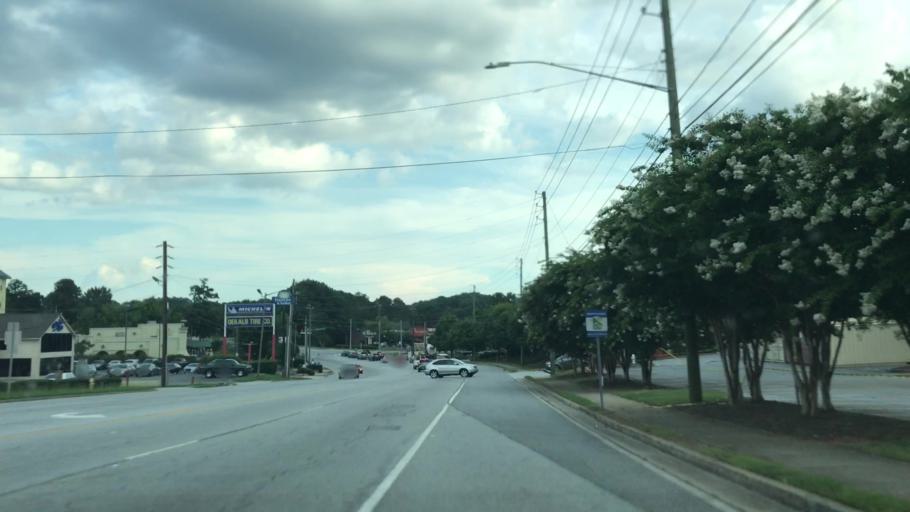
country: US
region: Georgia
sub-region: DeKalb County
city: Tucker
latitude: 33.8458
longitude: -84.2448
